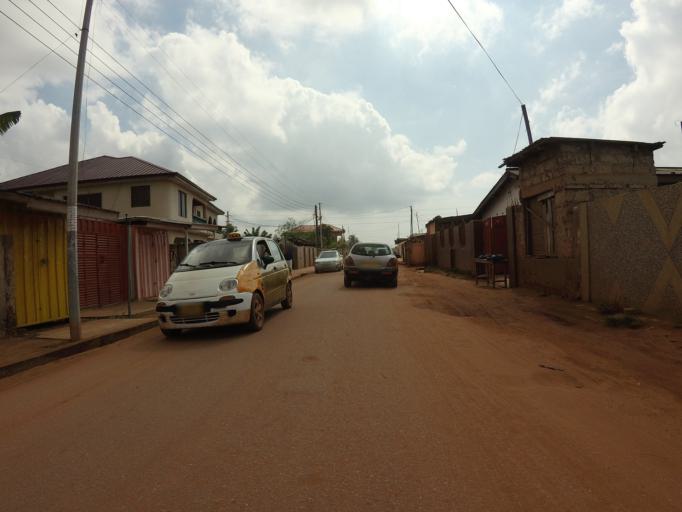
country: GH
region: Greater Accra
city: Nungua
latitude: 5.6190
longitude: -0.0938
